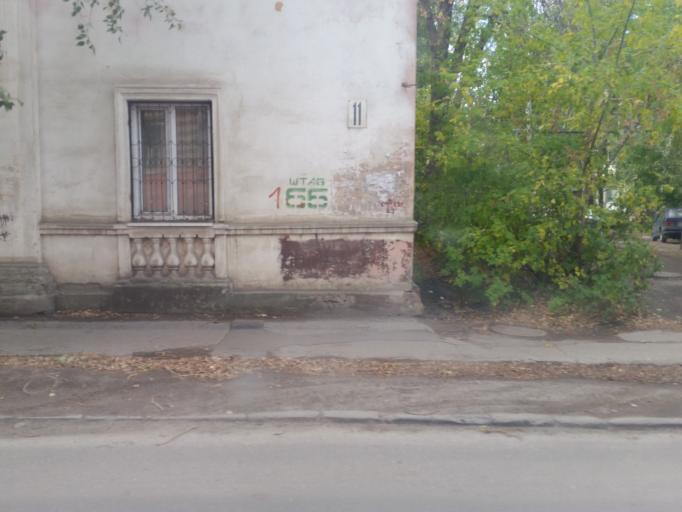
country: RU
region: Ulyanovsk
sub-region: Ulyanovskiy Rayon
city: Ulyanovsk
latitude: 54.3244
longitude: 48.3896
